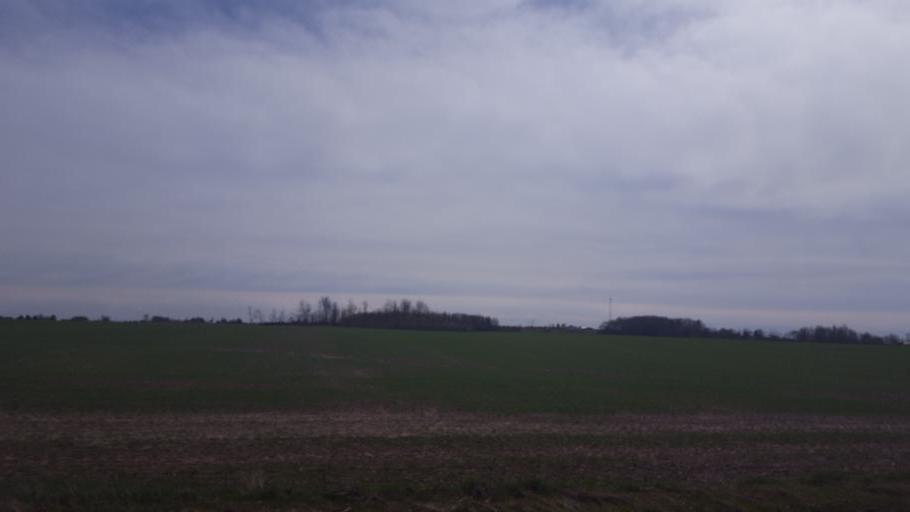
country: US
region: Michigan
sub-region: Gladwin County
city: Gladwin
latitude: 44.0308
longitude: -84.4763
